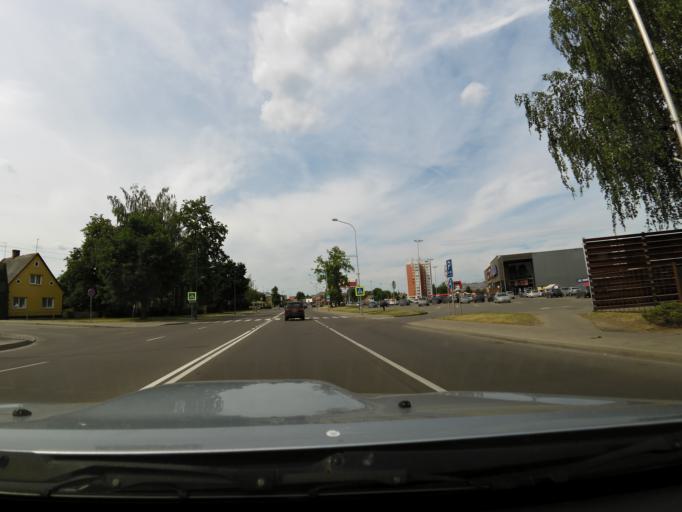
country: LT
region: Marijampoles apskritis
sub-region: Marijampole Municipality
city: Marijampole
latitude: 54.5588
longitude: 23.3542
